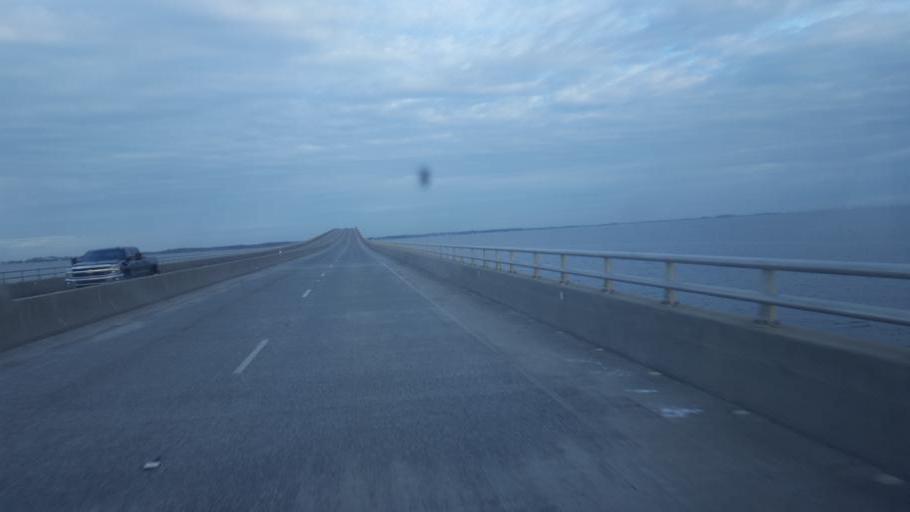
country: US
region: North Carolina
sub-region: Dare County
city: Manteo
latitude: 35.8845
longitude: -75.7075
